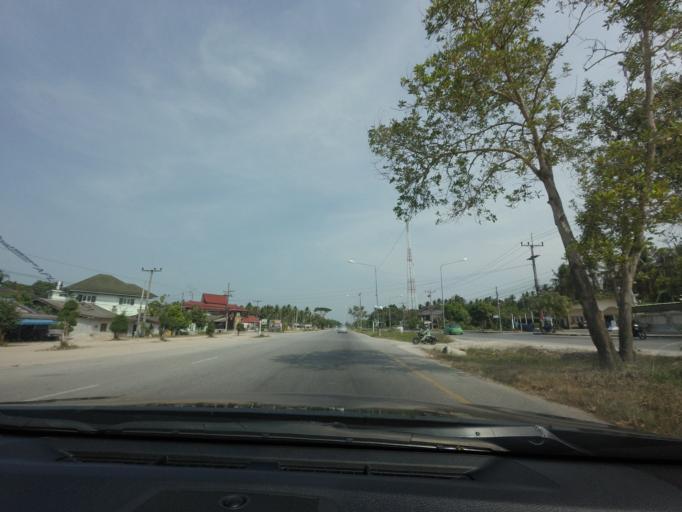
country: TH
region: Pattani
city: Mayo
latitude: 6.7986
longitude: 101.4328
